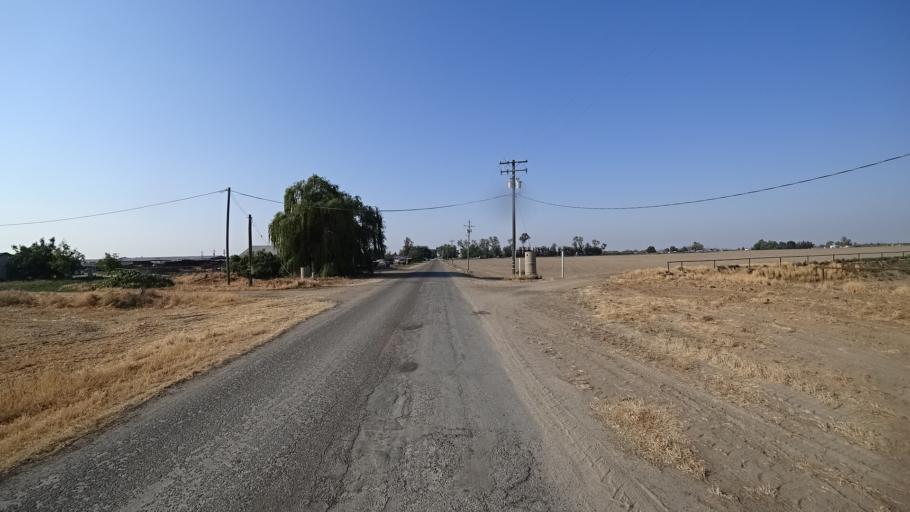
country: US
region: California
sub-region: Fresno County
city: Riverdale
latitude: 36.3787
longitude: -119.8431
